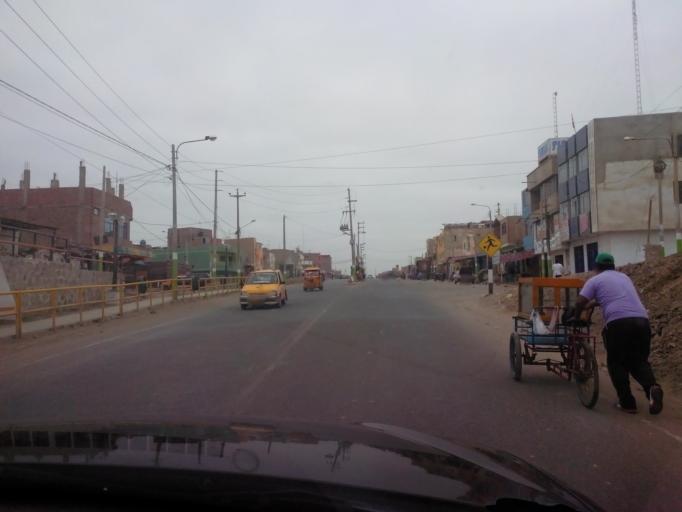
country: PE
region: Ica
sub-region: Provincia de Pisco
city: San Clemente
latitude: -13.6825
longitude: -76.1576
